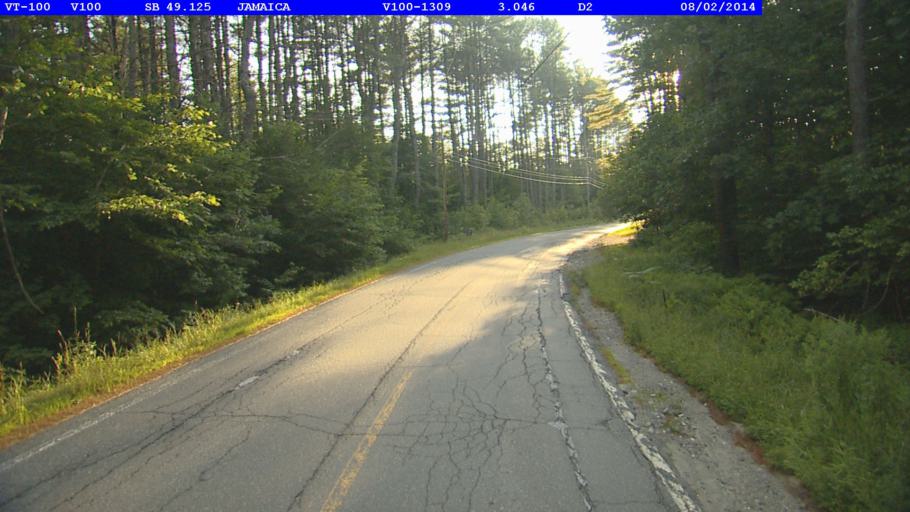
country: US
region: Vermont
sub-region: Windham County
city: Newfane
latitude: 43.0708
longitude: -72.7415
